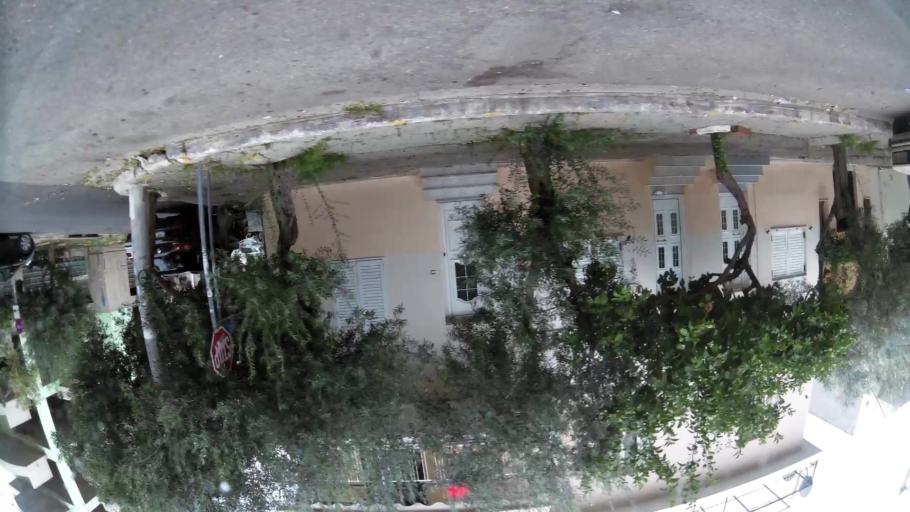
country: GR
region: Attica
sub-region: Nomarchia Athinas
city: Peristeri
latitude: 38.0035
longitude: 23.6913
